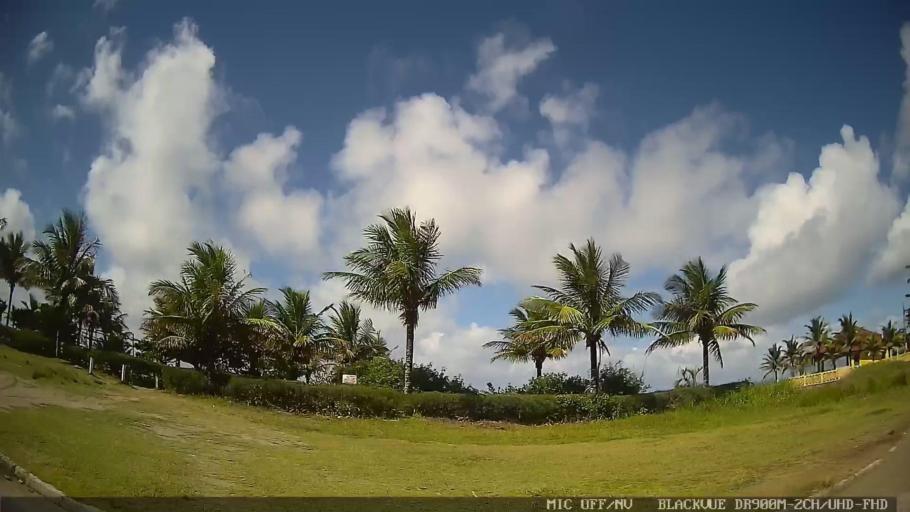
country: BR
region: Sao Paulo
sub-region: Itanhaem
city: Itanhaem
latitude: -24.2250
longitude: -46.8579
